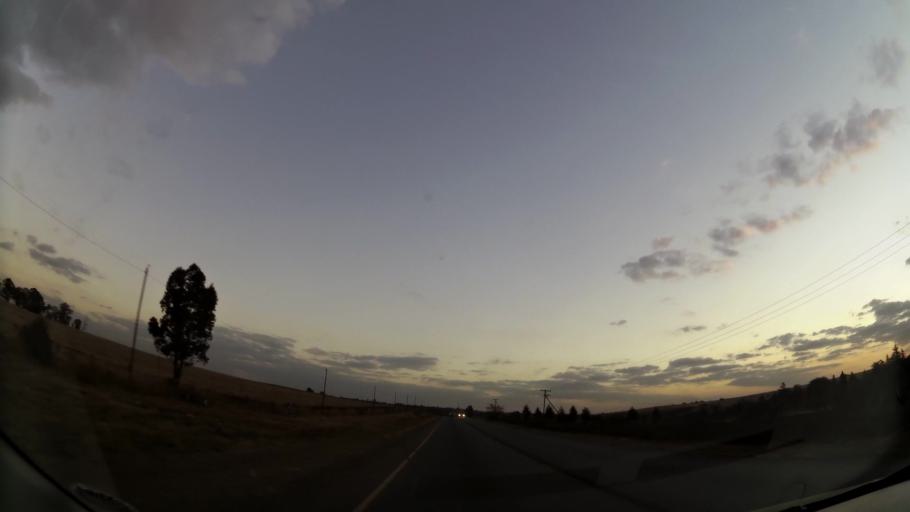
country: ZA
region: Gauteng
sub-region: West Rand District Municipality
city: Krugersdorp
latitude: -26.0579
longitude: 27.7039
